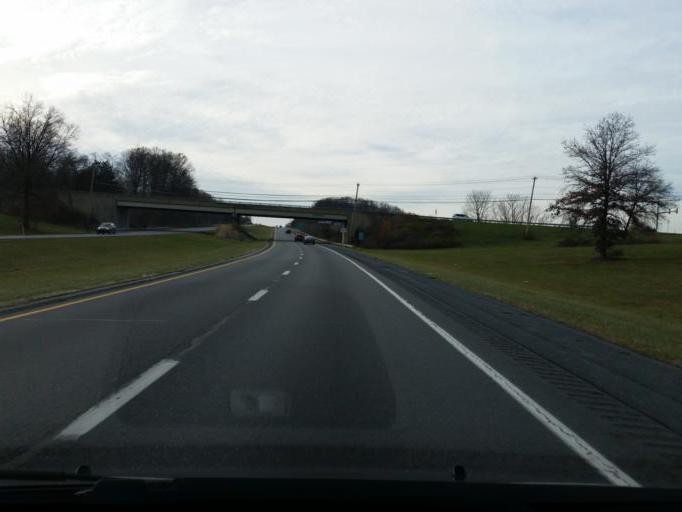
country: US
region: Pennsylvania
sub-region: Dauphin County
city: Middletown
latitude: 40.2273
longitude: -76.7353
